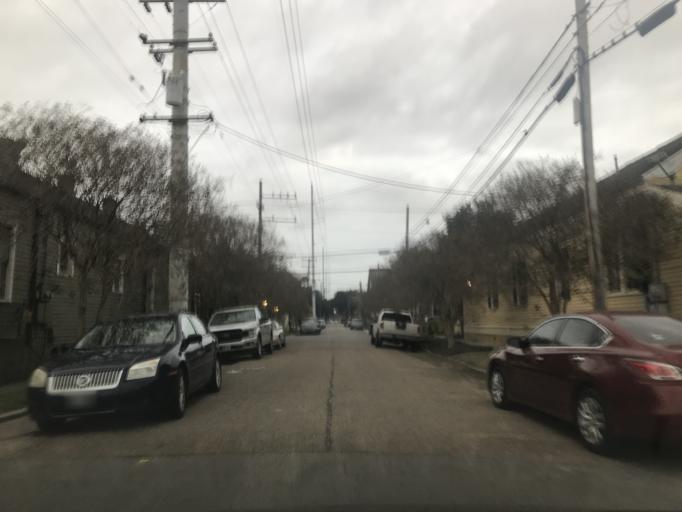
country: US
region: Louisiana
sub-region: Orleans Parish
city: New Orleans
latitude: 29.9655
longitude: -90.0956
